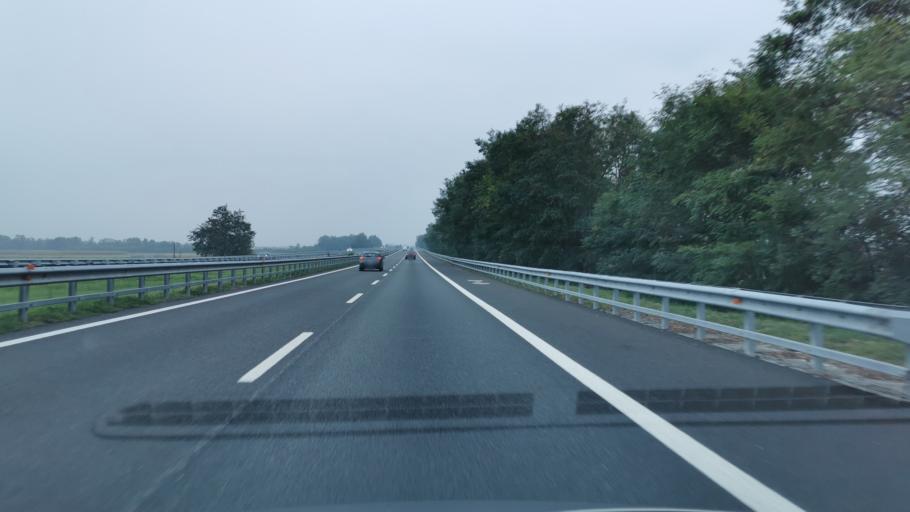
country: IT
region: Piedmont
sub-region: Provincia di Cuneo
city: Caramagna Piemonte
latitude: 44.8047
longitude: 7.7524
